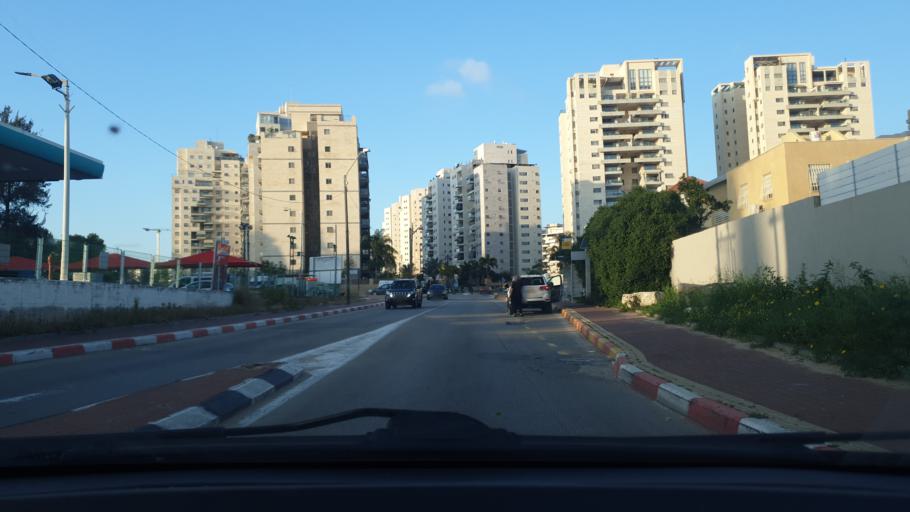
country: IL
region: Central District
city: Ness Ziona
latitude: 31.9359
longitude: 34.8317
